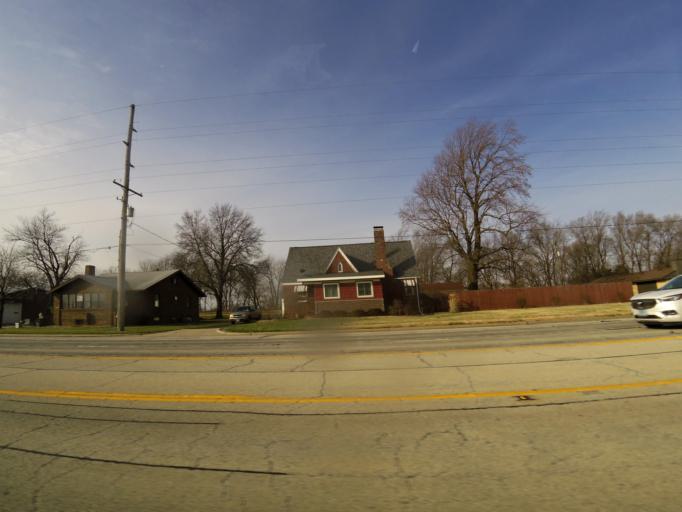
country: US
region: Illinois
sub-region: Macon County
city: Macon
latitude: 39.7770
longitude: -88.9798
